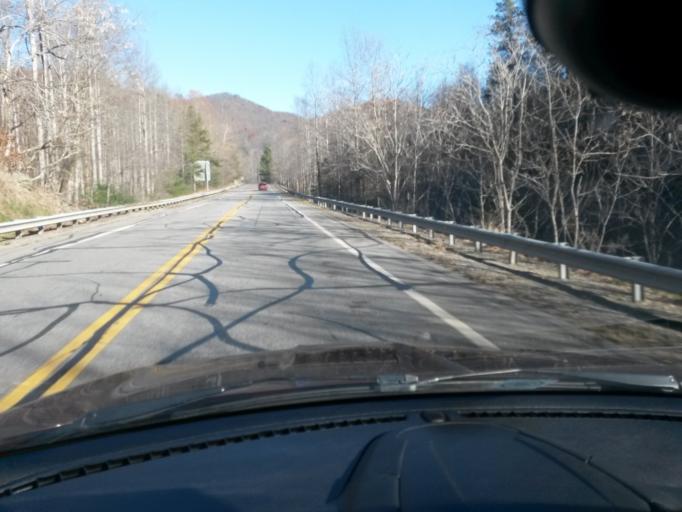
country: US
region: Virginia
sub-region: Patrick County
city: Stuart
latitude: 36.6632
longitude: -80.2750
